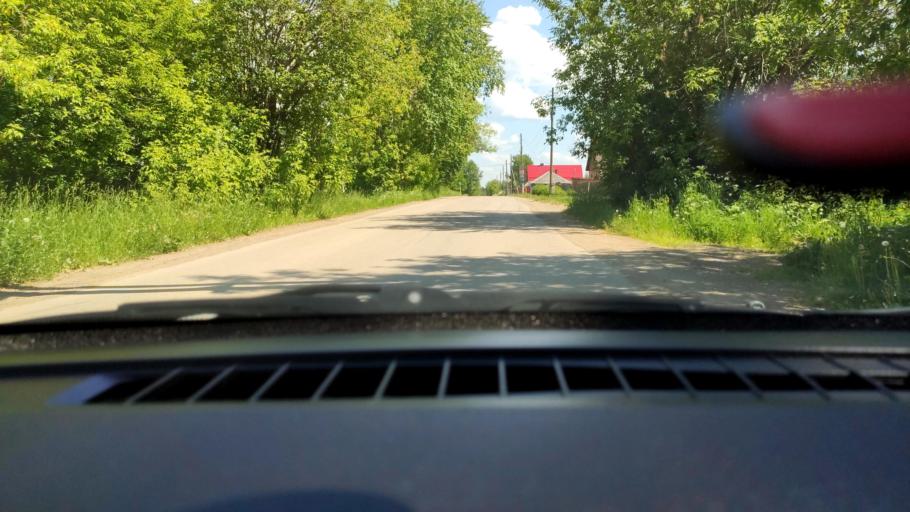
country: RU
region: Perm
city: Sylva
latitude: 58.0335
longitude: 56.7604
